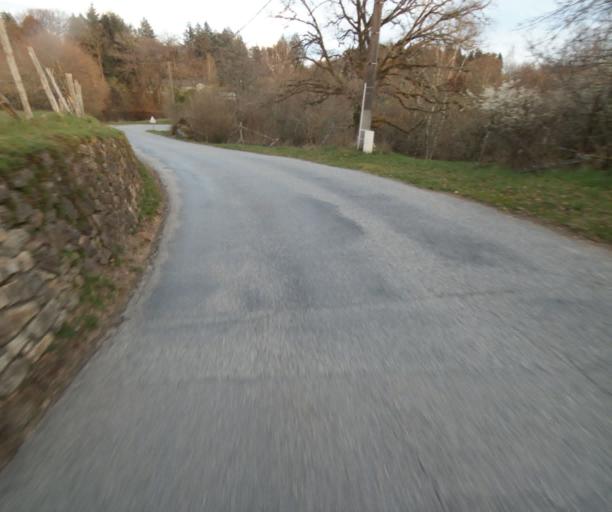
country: FR
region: Limousin
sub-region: Departement de la Correze
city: Correze
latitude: 45.2763
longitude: 1.9736
